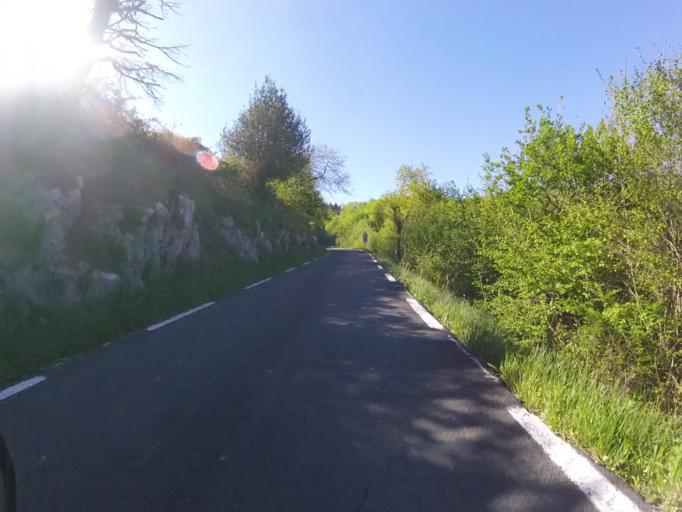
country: ES
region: Basque Country
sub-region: Provincia de Guipuzcoa
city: Aizarnazabal
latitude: 43.2202
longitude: -2.2126
